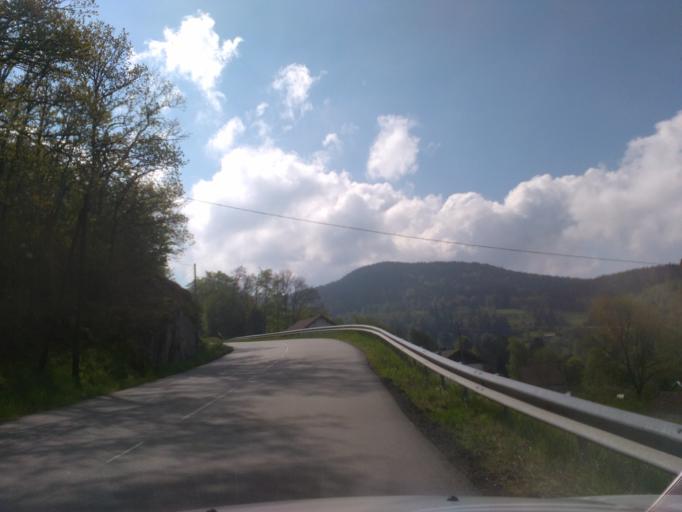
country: FR
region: Lorraine
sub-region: Departement des Vosges
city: Vagney
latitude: 47.9945
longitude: 6.7357
